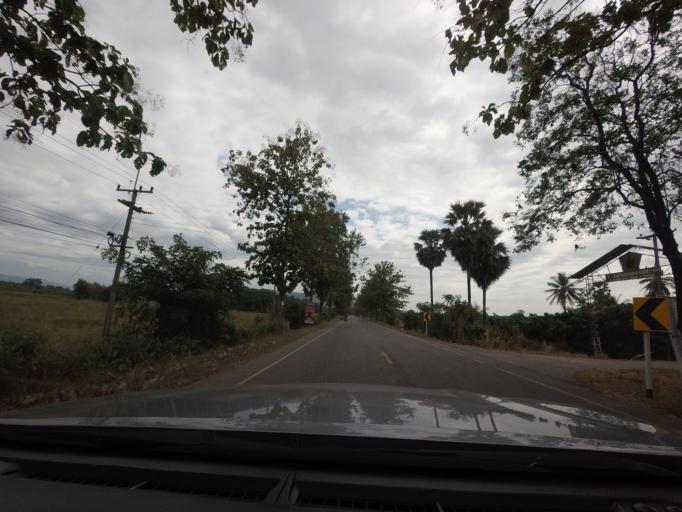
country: TH
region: Phitsanulok
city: Wang Thong
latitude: 16.6955
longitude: 100.5201
